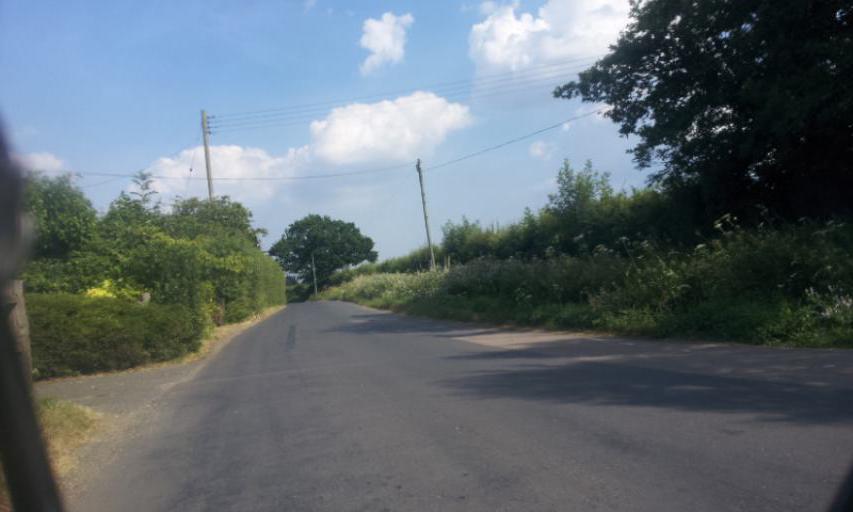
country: GB
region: England
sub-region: Kent
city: Yalding
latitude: 51.2031
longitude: 0.4256
